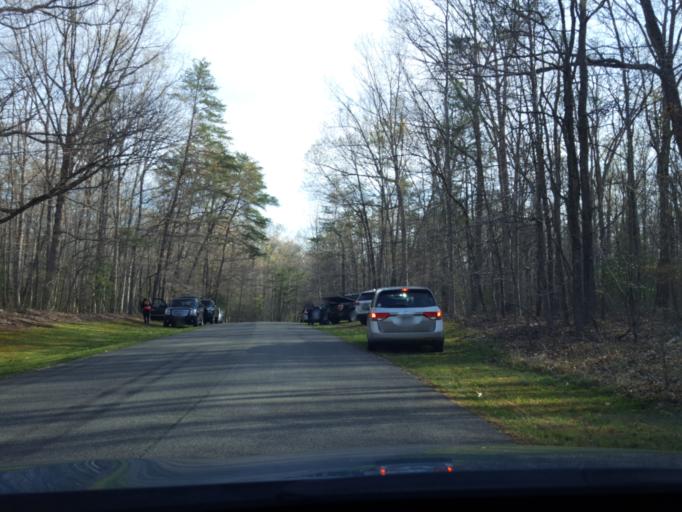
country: US
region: Maryland
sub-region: Prince George's County
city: Croom
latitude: 38.7675
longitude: -76.7197
